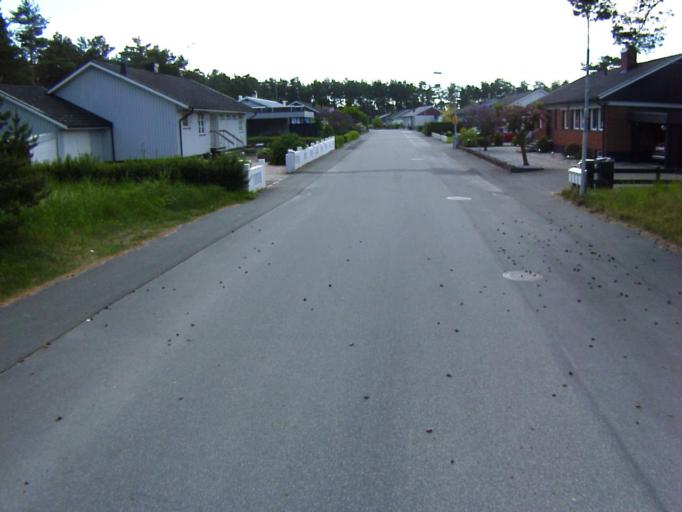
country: SE
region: Skane
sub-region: Kristianstads Kommun
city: Ahus
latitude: 55.9457
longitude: 14.2749
